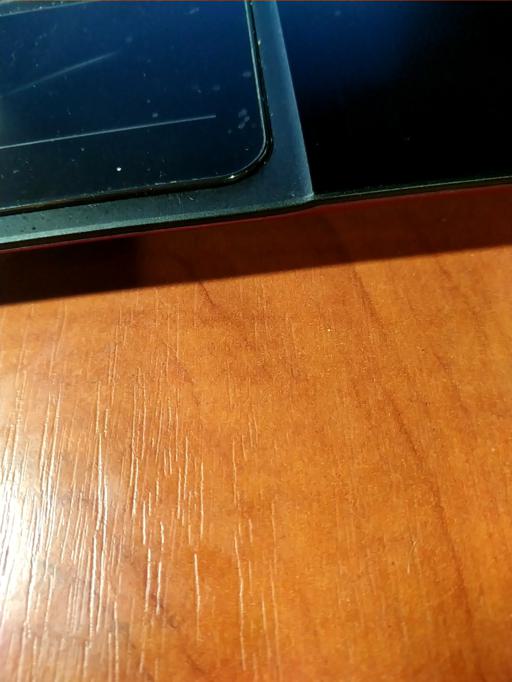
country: RU
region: Tverskaya
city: Zubtsov
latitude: 56.3309
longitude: 34.6740
